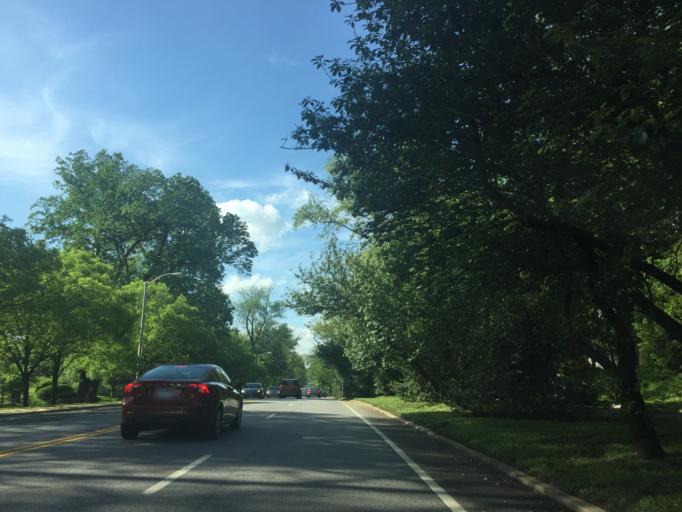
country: US
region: Maryland
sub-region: Baltimore County
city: Towson
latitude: 39.3533
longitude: -76.6433
